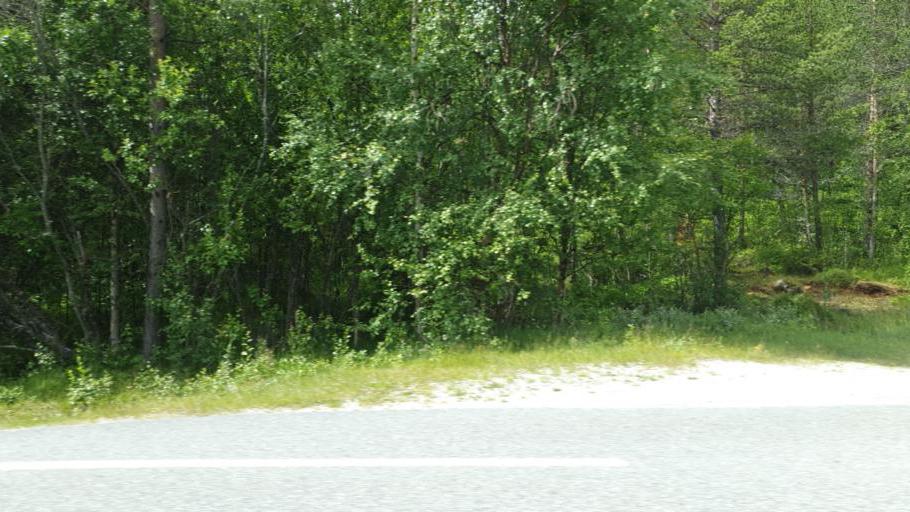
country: NO
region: Oppland
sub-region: Vaga
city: Vagamo
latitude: 61.7414
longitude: 9.0913
